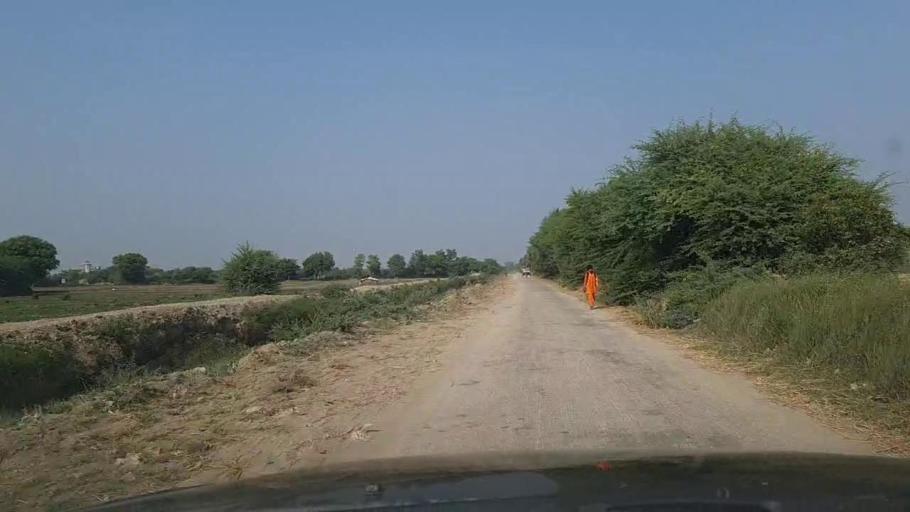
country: PK
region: Sindh
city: Mirpur Batoro
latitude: 24.7189
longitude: 68.2553
